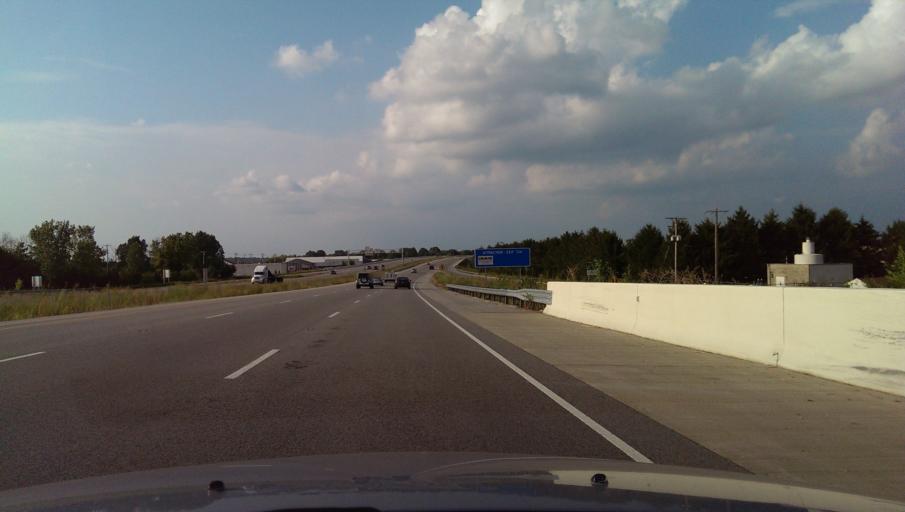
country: US
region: Indiana
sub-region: Hamilton County
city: Westfield
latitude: 40.0438
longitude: -86.1357
